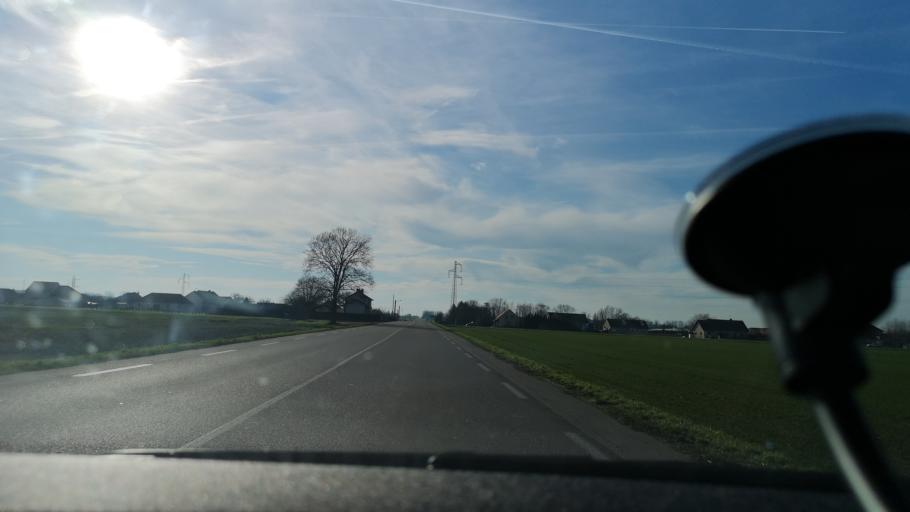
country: FR
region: Bourgogne
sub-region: Departement de Saone-et-Loire
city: Sassenay
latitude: 46.8108
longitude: 4.9527
